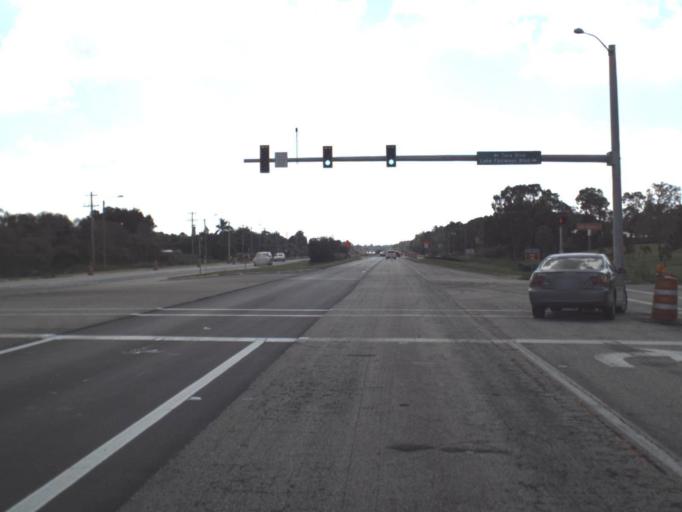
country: US
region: Florida
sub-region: Lee County
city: Suncoast Estates
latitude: 26.7462
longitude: -81.9183
